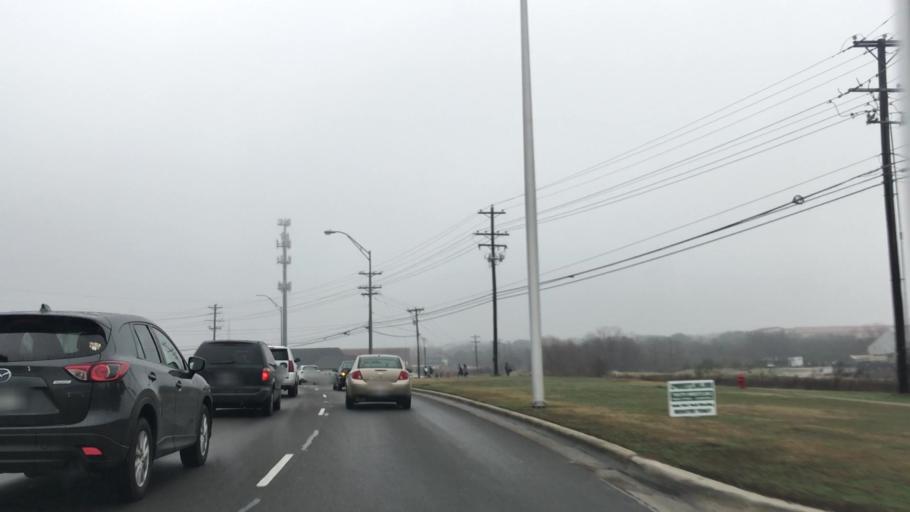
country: US
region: Texas
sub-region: Williamson County
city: Cedar Park
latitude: 30.4768
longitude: -97.8356
